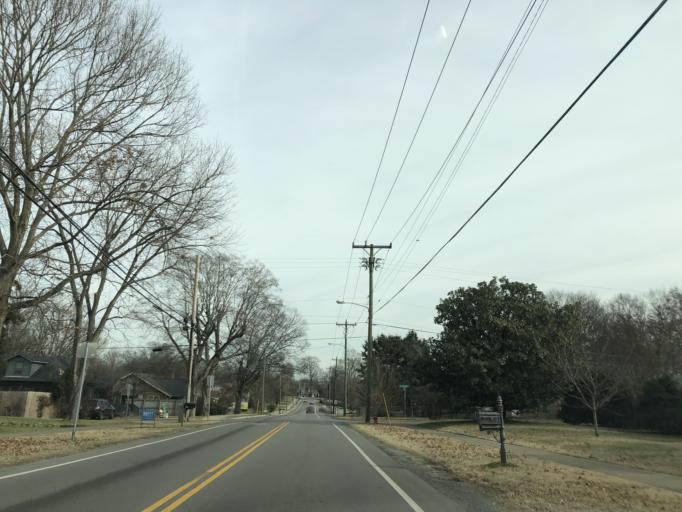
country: US
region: Tennessee
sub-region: Davidson County
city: Nashville
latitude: 36.2104
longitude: -86.7291
